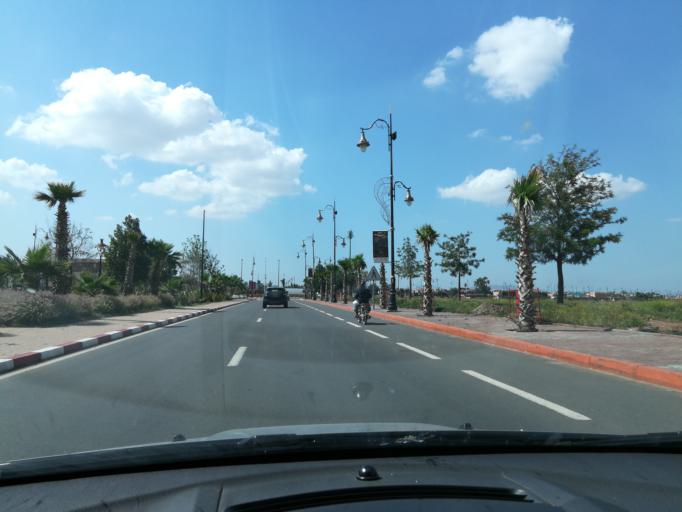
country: MA
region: Marrakech-Tensift-Al Haouz
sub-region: Marrakech
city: Marrakesh
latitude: 31.6026
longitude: -7.9980
